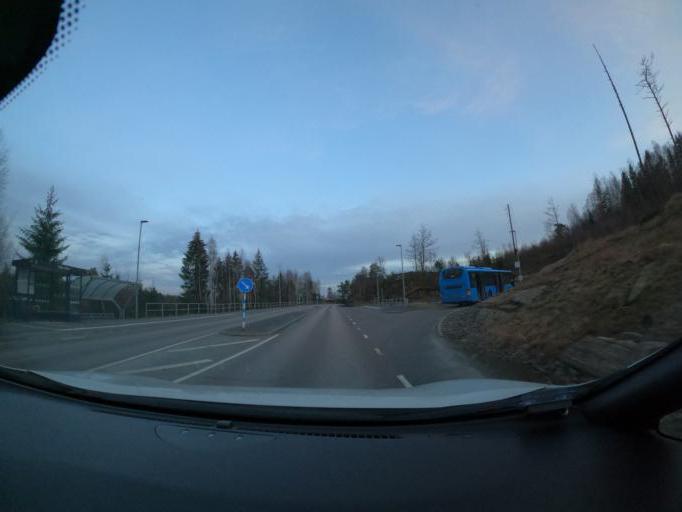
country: SE
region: Vaestra Goetaland
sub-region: Harryda Kommun
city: Molnlycke
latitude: 57.6496
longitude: 12.1568
